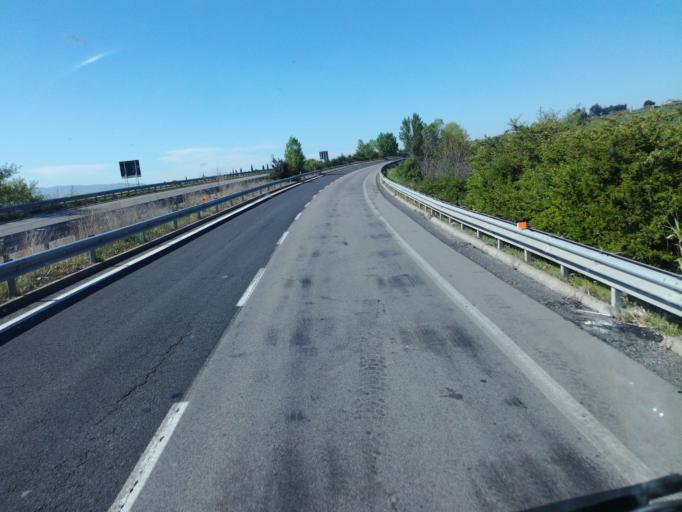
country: IT
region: Umbria
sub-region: Provincia di Perugia
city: Petrignano
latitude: 43.1129
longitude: 12.5066
